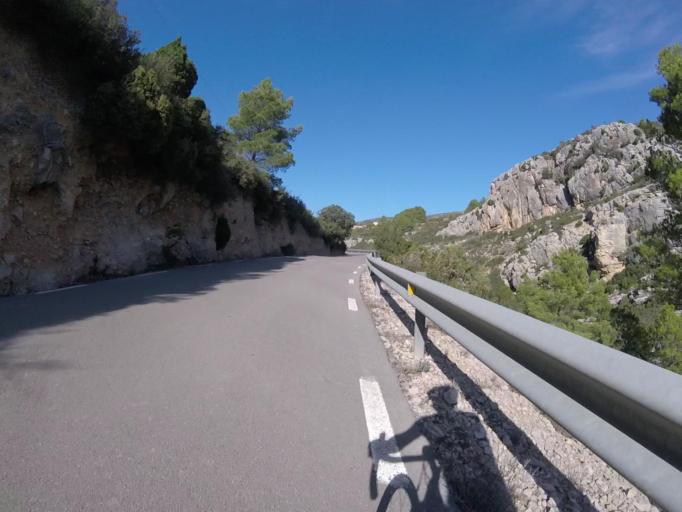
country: ES
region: Valencia
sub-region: Provincia de Castello
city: Sarratella
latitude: 40.2720
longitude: 0.0449
